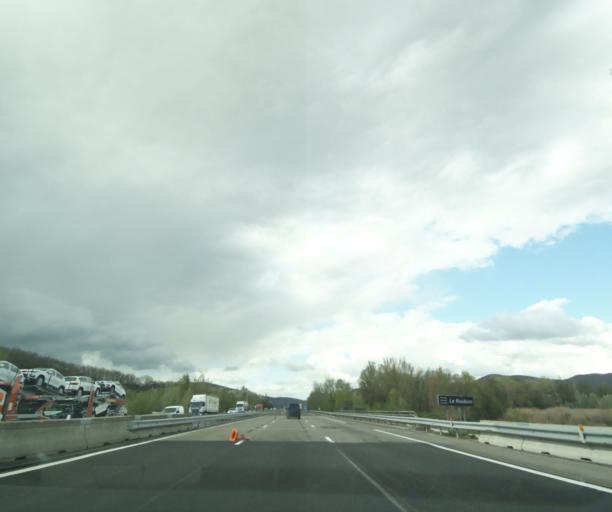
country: FR
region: Rhone-Alpes
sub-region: Departement de la Drome
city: Saint-Marcel-les-Sauzet
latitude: 44.5833
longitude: 4.8040
